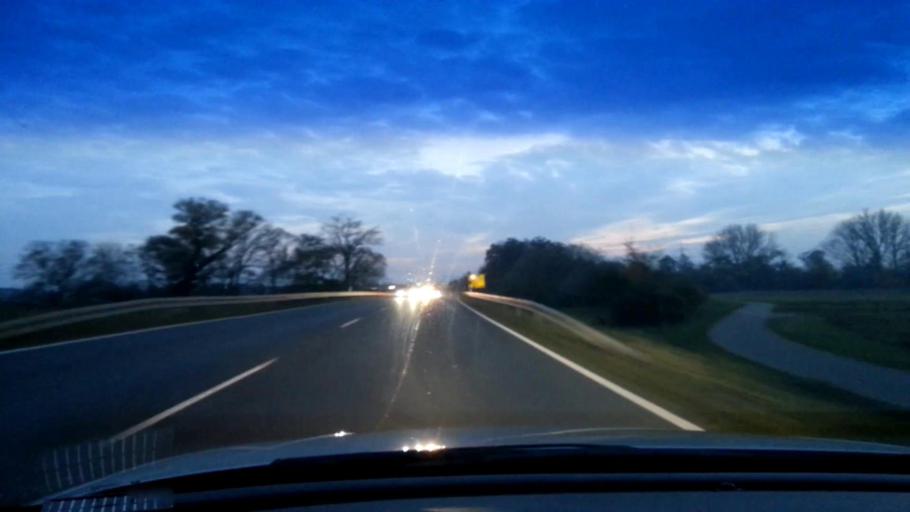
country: DE
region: Bavaria
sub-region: Upper Franconia
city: Kemmern
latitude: 49.9413
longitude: 10.8852
